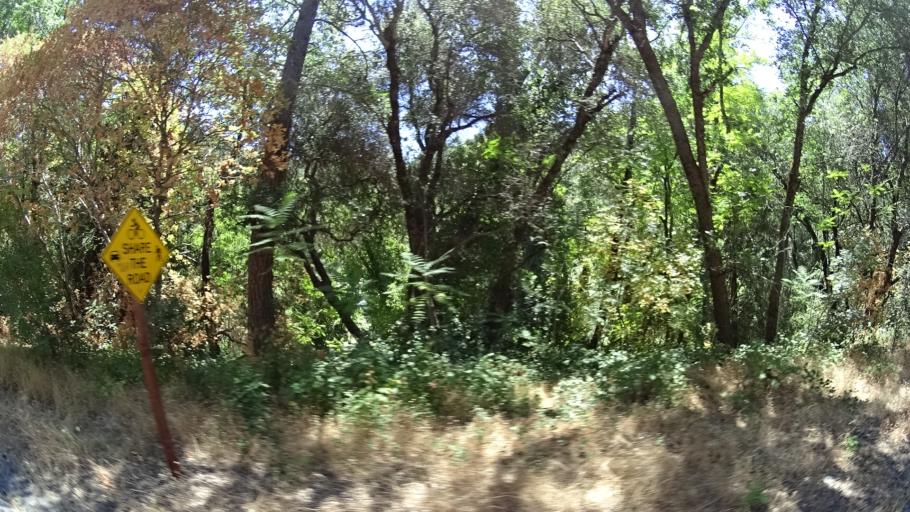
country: US
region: California
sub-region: Calaveras County
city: Murphys
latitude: 38.1200
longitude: -120.4972
